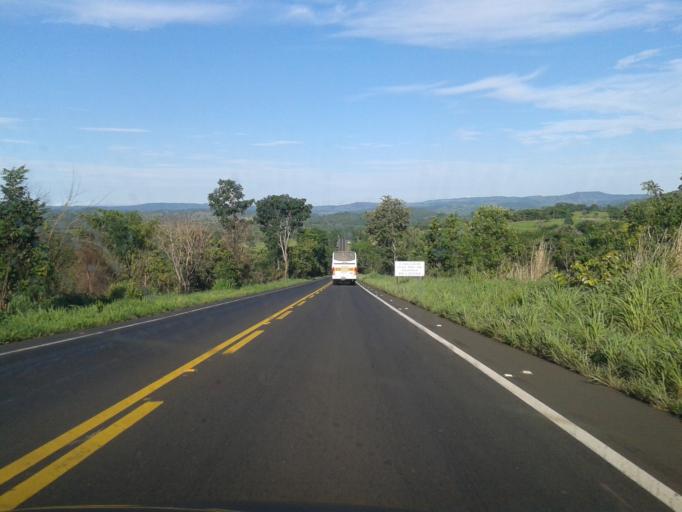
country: BR
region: Goias
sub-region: Caldas Novas
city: Caldas Novas
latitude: -18.1163
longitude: -48.6030
